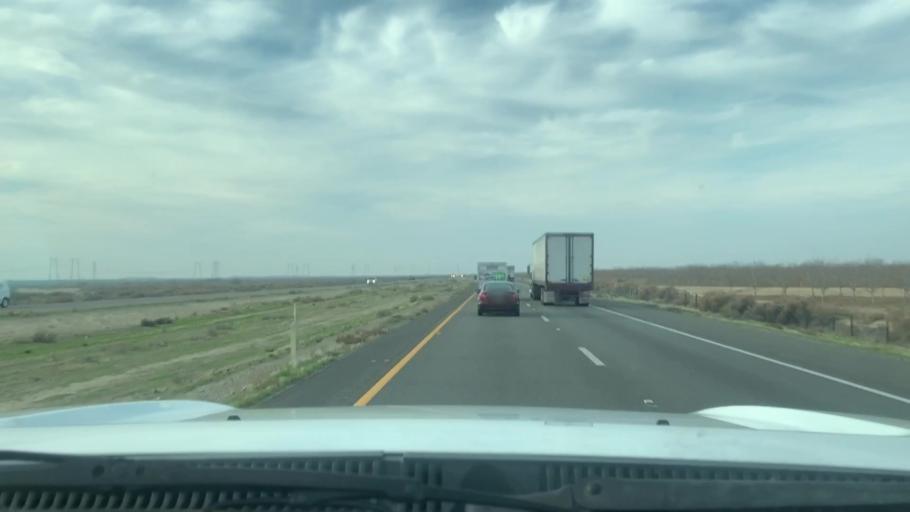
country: US
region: California
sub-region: Kern County
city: Buttonwillow
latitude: 35.4708
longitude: -119.4958
